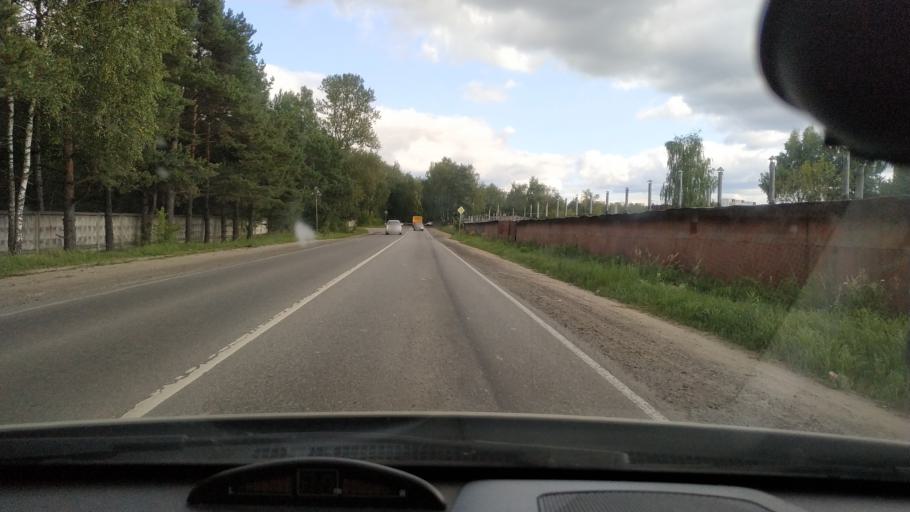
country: RU
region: Moskovskaya
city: Chornaya
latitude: 55.7654
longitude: 38.0682
